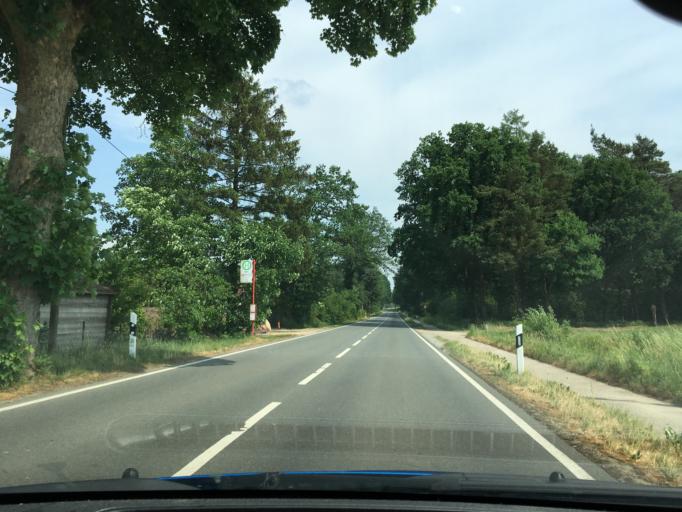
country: DE
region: Lower Saxony
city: Jesteburg
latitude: 53.2719
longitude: 9.9261
